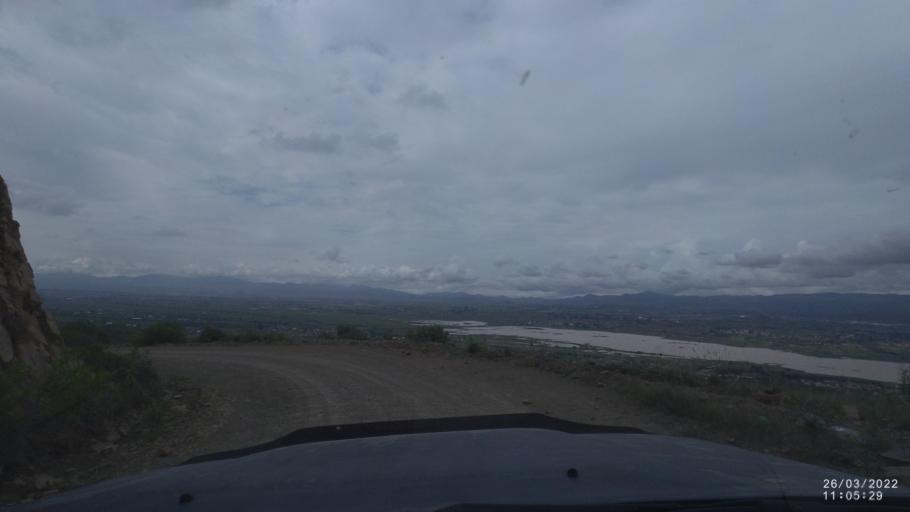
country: BO
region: Cochabamba
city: Tarata
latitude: -17.5320
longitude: -66.0226
